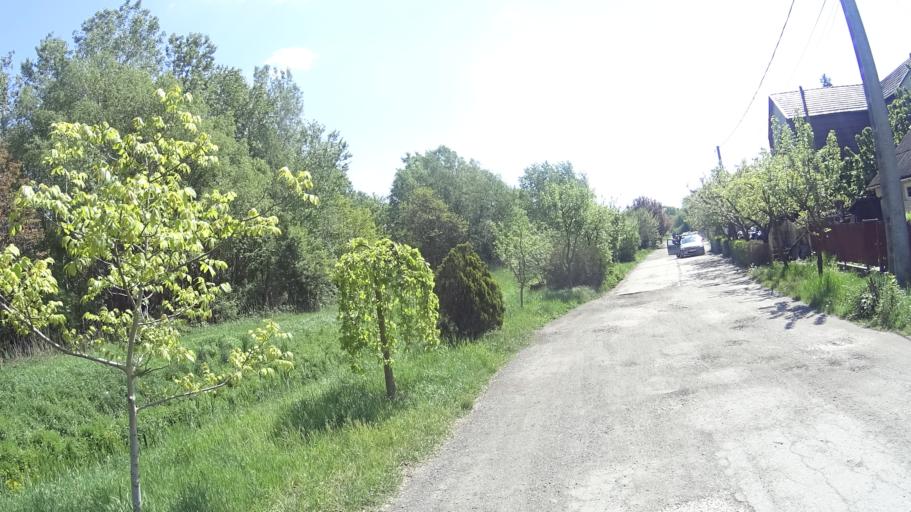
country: HU
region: Budapest
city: Budapest XXIII. keruelet
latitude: 47.3857
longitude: 19.1559
